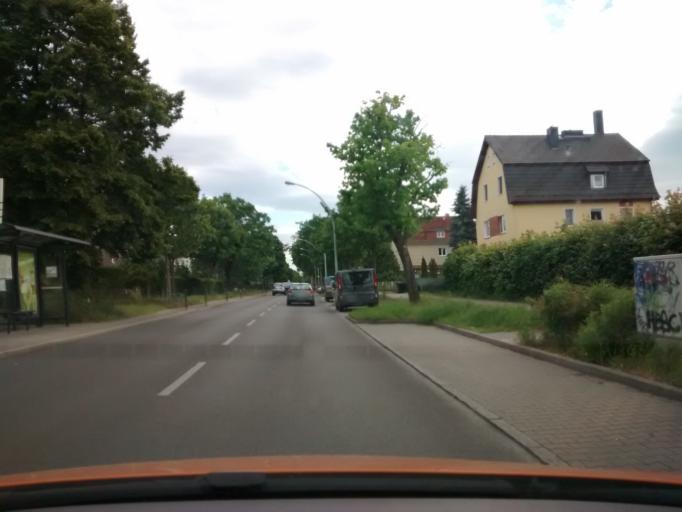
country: DE
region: Berlin
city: Bohnsdorf
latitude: 52.3943
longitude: 13.5733
